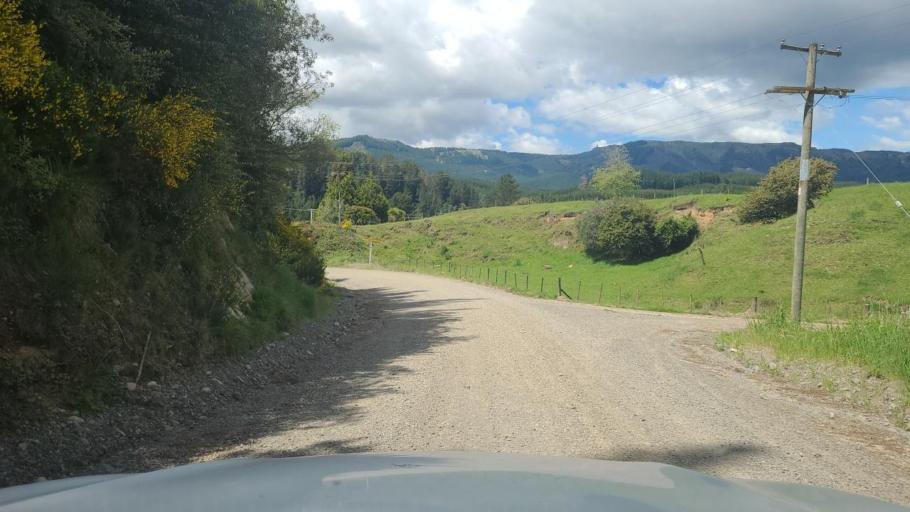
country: NZ
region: Hawke's Bay
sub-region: Napier City
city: Taradale
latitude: -39.1807
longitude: 176.6315
